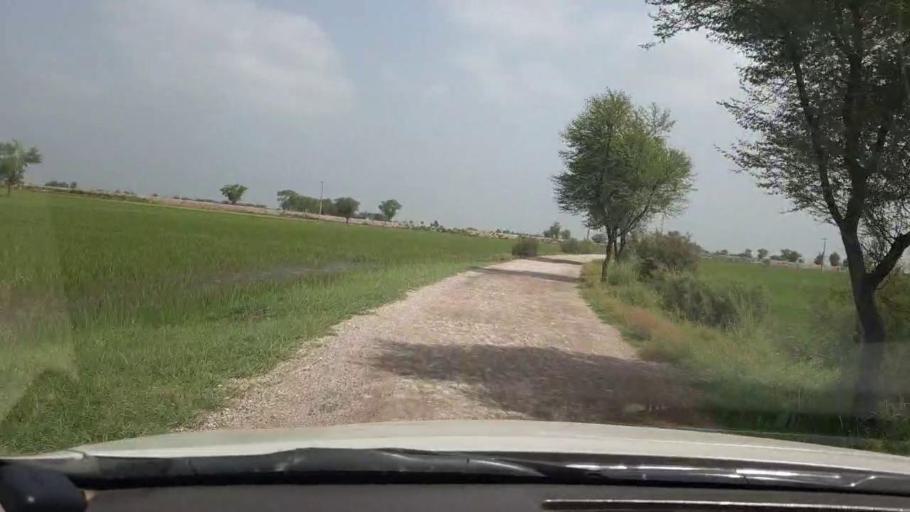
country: PK
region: Sindh
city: Garhi Yasin
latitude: 28.0105
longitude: 68.5395
